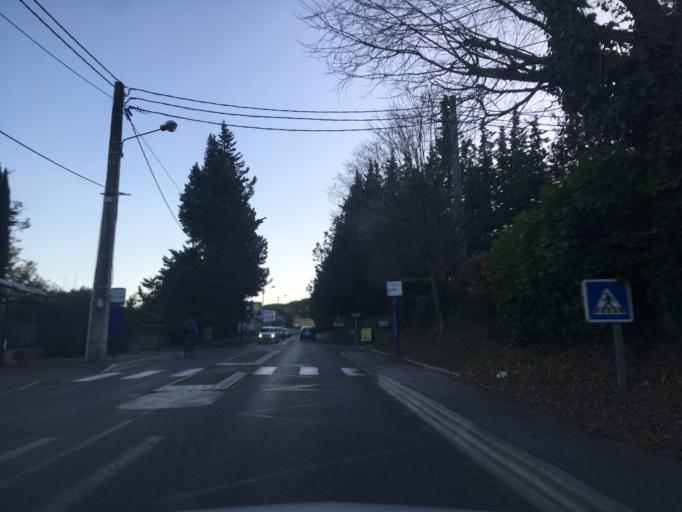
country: FR
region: Provence-Alpes-Cote d'Azur
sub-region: Departement des Alpes-Maritimes
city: Peymeinade
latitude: 43.6379
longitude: 6.8648
